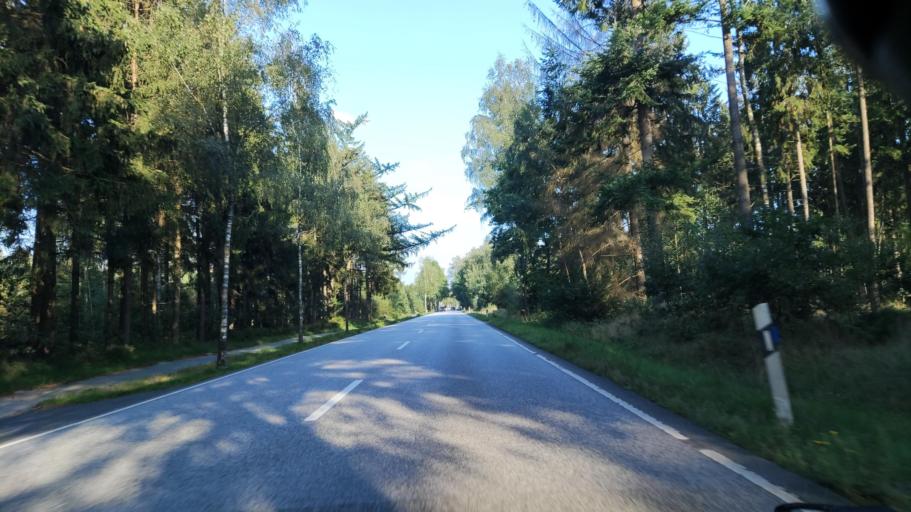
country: DE
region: Schleswig-Holstein
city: Bad Bramstedt
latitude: 53.9052
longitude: 9.9158
